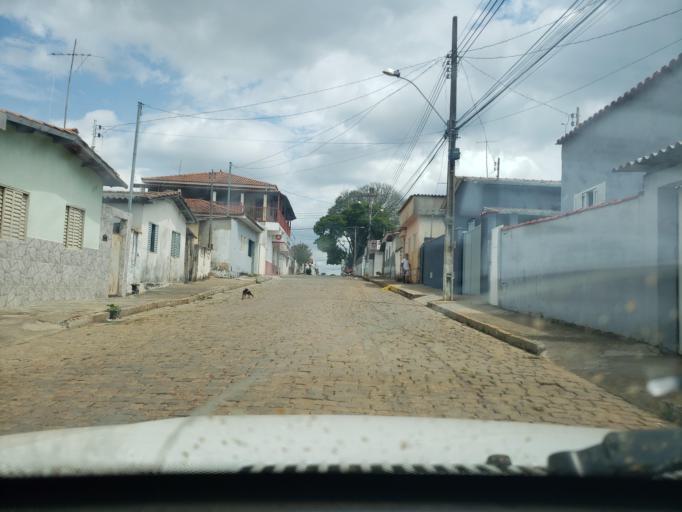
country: BR
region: Minas Gerais
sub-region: Boa Esperanca
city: Boa Esperanca
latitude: -21.0812
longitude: -45.5760
